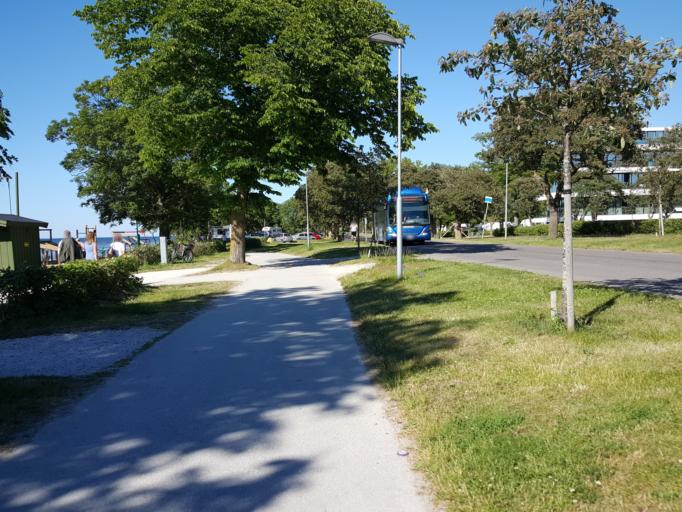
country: SE
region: Gotland
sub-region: Gotland
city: Visby
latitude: 57.6531
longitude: 18.3041
